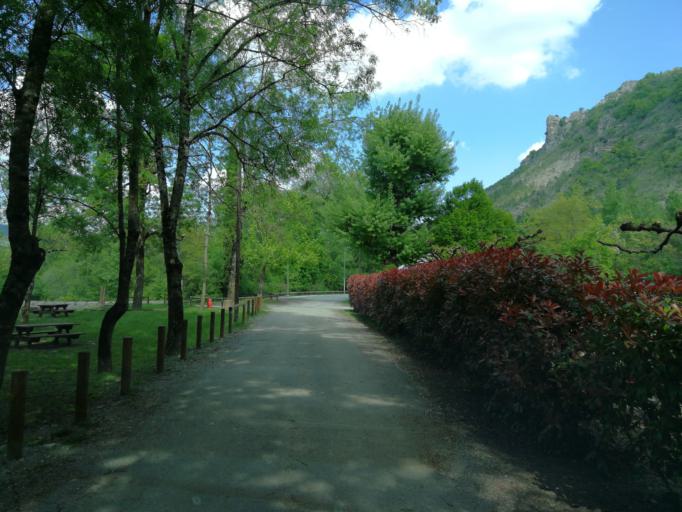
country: FR
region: Rhone-Alpes
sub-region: Departement de l'Ardeche
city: Flaviac
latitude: 44.7432
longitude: 4.6700
